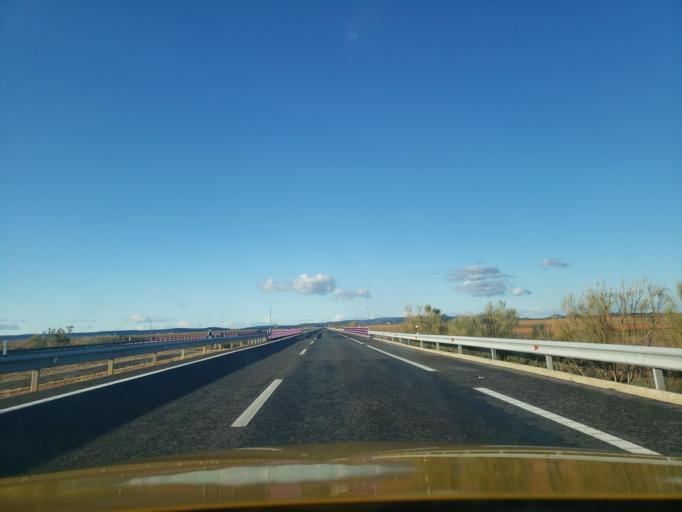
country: ES
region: Castille-La Mancha
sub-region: Province of Toledo
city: Consuegra
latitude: 39.5298
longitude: -3.6592
